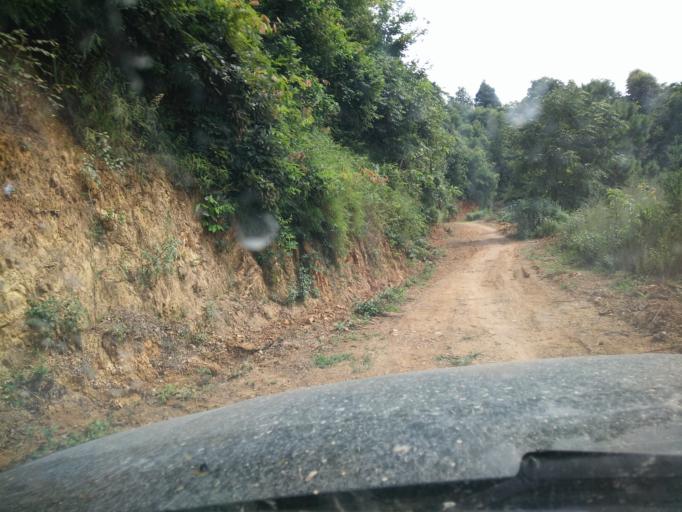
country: CN
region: Guangxi Zhuangzu Zizhiqu
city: Leli
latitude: 24.7733
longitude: 105.9092
